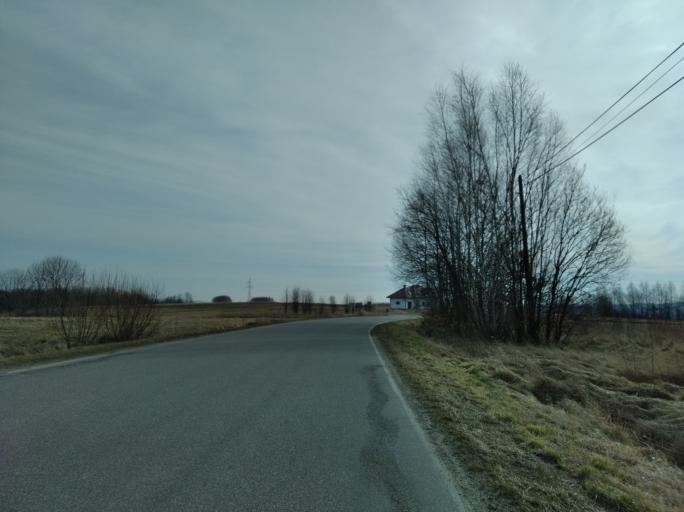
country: PL
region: Subcarpathian Voivodeship
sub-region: Powiat brzozowski
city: Jasienica Rosielna
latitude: 49.7448
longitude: 21.9418
